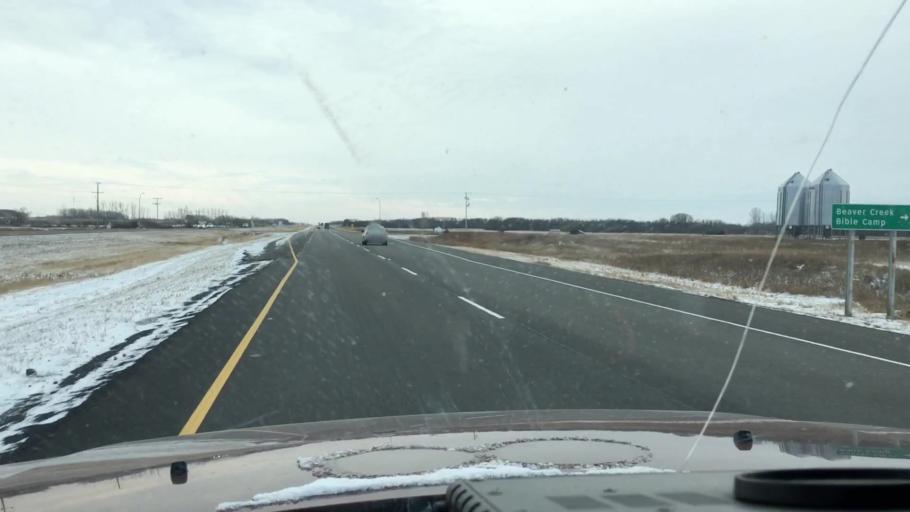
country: CA
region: Saskatchewan
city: Saskatoon
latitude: 52.0001
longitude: -106.5681
